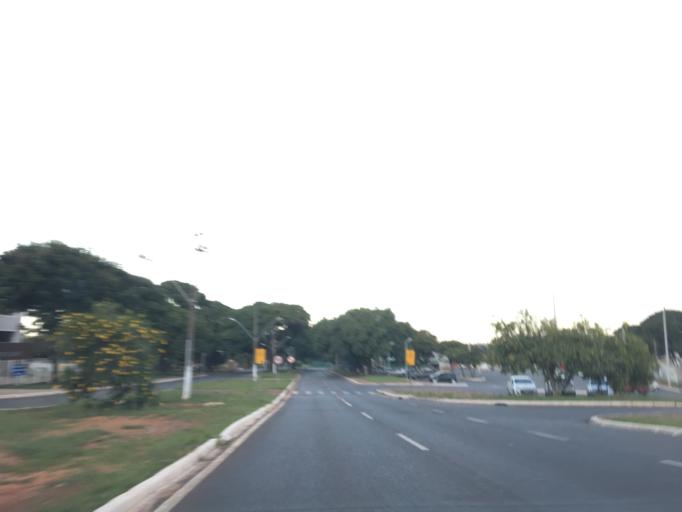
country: BR
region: Federal District
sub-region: Brasilia
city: Brasilia
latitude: -15.8255
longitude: -47.9736
